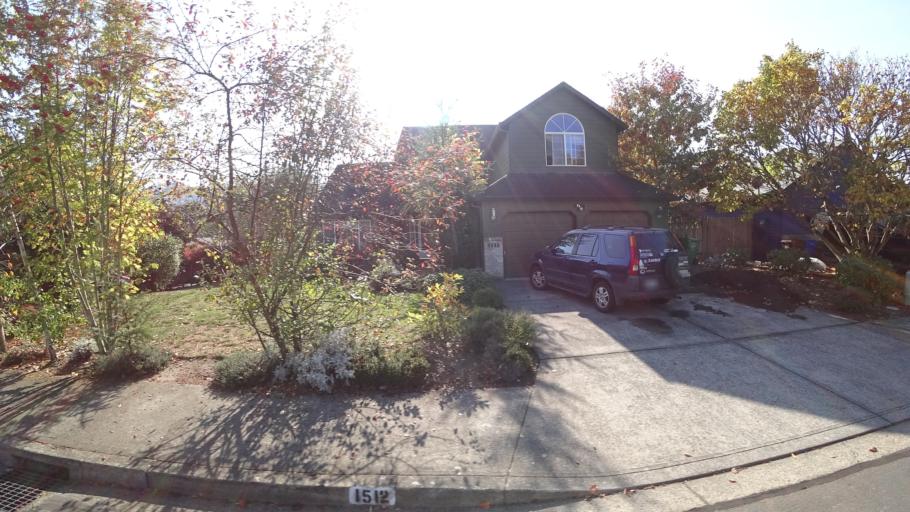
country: US
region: Oregon
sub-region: Multnomah County
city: Gresham
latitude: 45.4964
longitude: -122.4474
